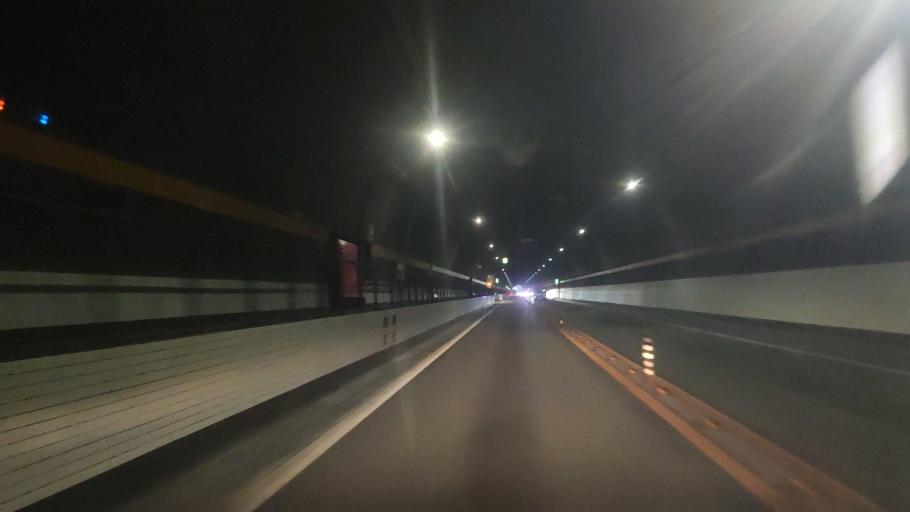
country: JP
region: Nagasaki
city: Nagasaki-shi
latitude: 32.7783
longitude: 129.8870
